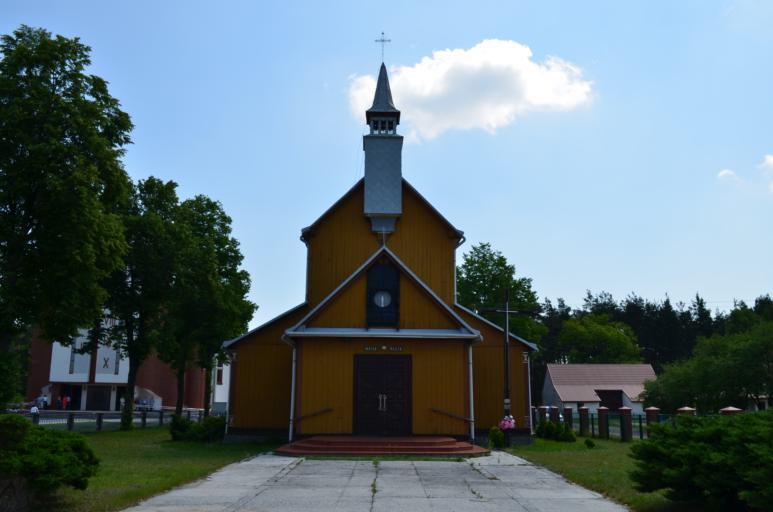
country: PL
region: Subcarpathian Voivodeship
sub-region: Powiat nizanski
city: Konczyce
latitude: 50.4479
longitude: 22.1543
